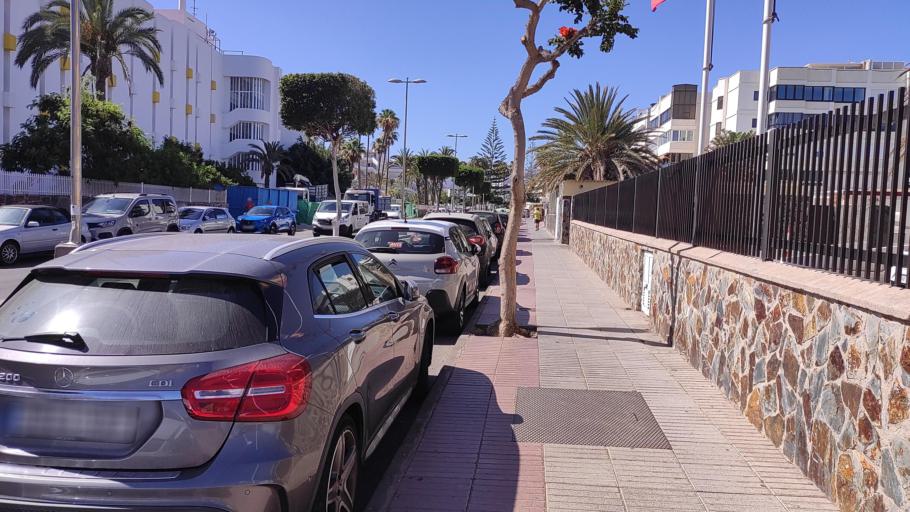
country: ES
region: Canary Islands
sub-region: Provincia de Las Palmas
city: Playa del Ingles
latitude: 27.7496
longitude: -15.5767
